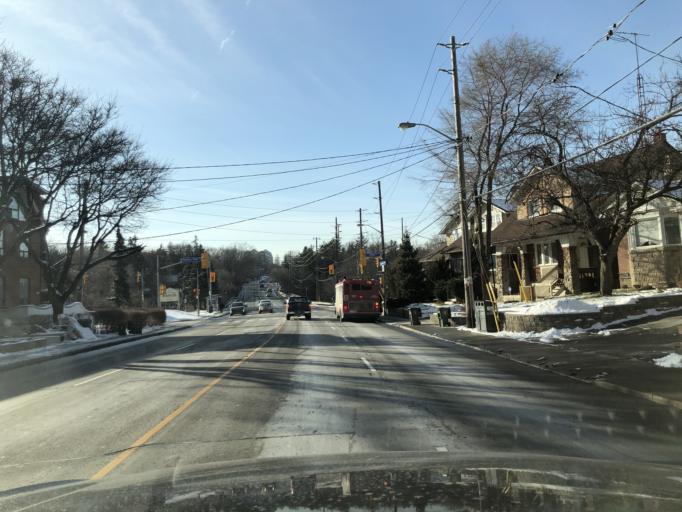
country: CA
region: Ontario
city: Etobicoke
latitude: 43.6996
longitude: -79.5190
